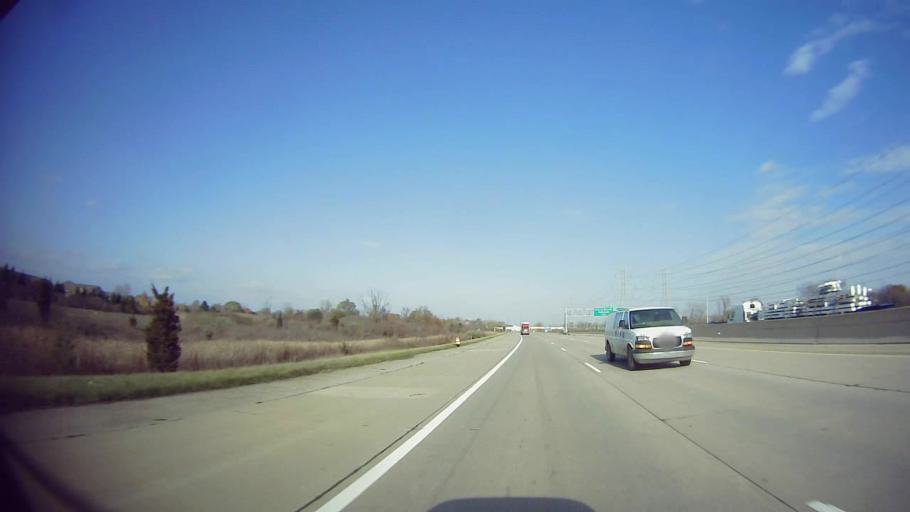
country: US
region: Michigan
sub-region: Monroe County
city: South Rockwood
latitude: 42.0613
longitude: -83.2598
